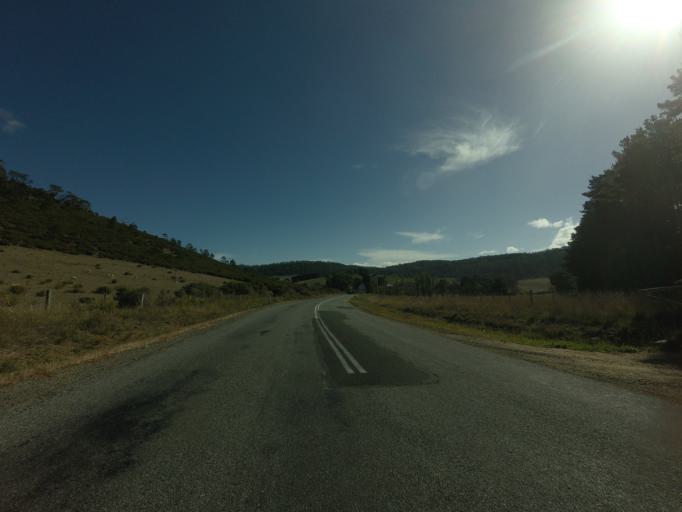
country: AU
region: Tasmania
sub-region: Break O'Day
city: St Helens
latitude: -41.9563
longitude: 148.1657
